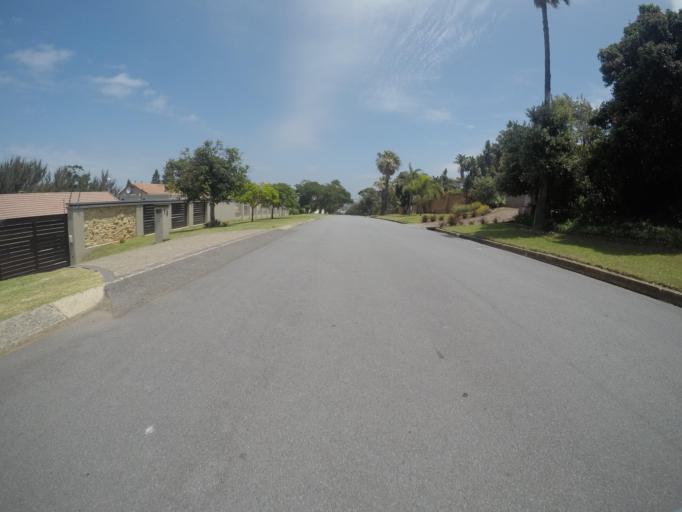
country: ZA
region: Eastern Cape
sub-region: Buffalo City Metropolitan Municipality
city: East London
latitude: -32.9991
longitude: 27.9296
